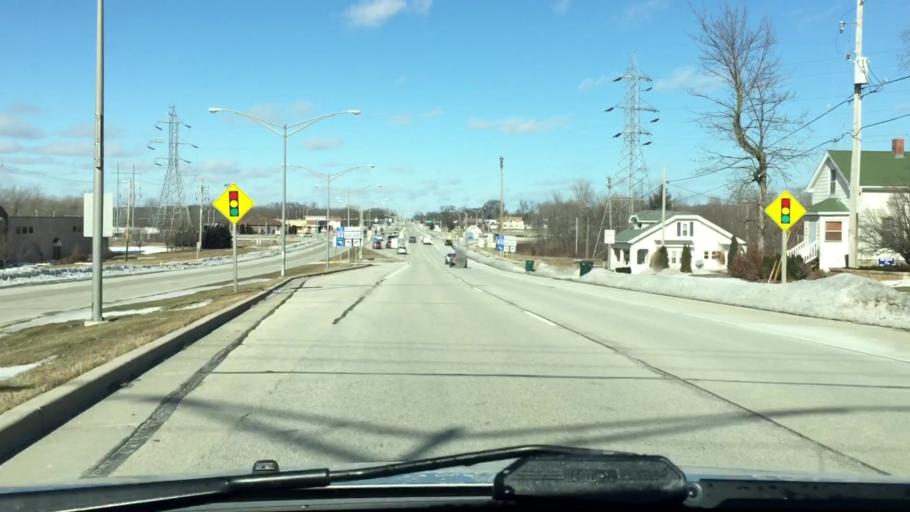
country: US
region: Wisconsin
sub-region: Milwaukee County
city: South Milwaukee
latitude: 42.9129
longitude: -87.9109
